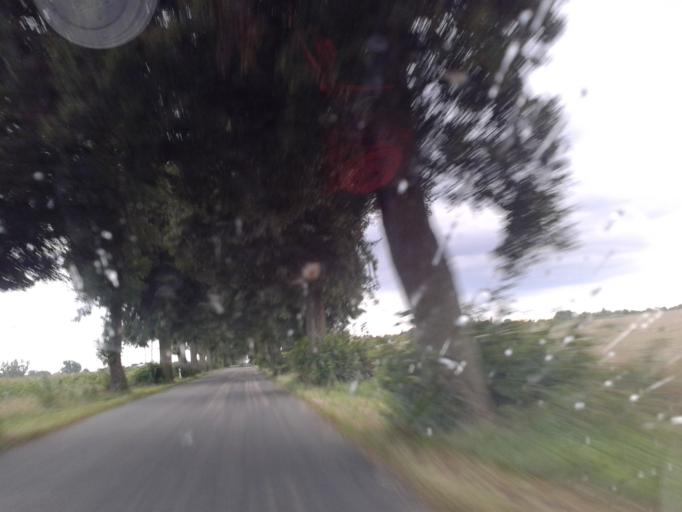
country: PL
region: West Pomeranian Voivodeship
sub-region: Powiat szczecinecki
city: Grzmiaca
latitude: 53.8424
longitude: 16.4451
